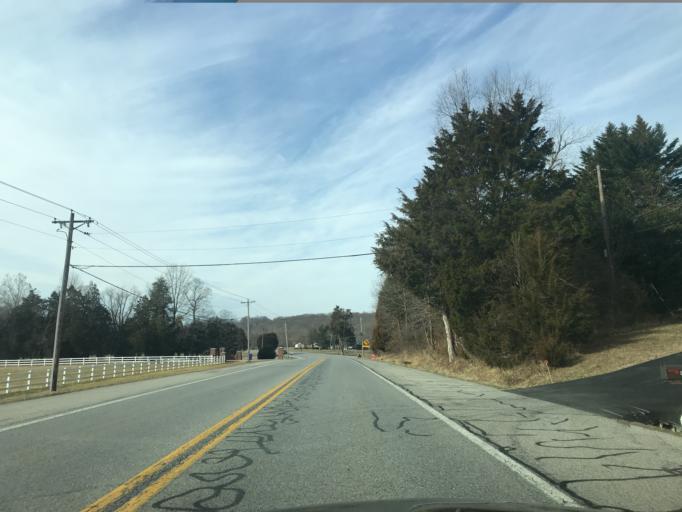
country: US
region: Maryland
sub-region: Charles County
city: La Plata
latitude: 38.5225
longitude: -77.0091
